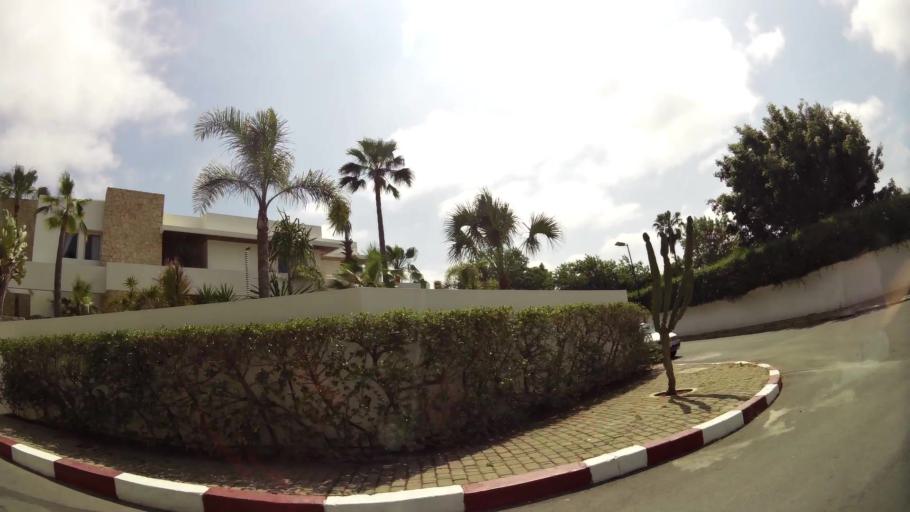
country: MA
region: Rabat-Sale-Zemmour-Zaer
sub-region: Rabat
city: Rabat
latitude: 33.9809
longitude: -6.8368
